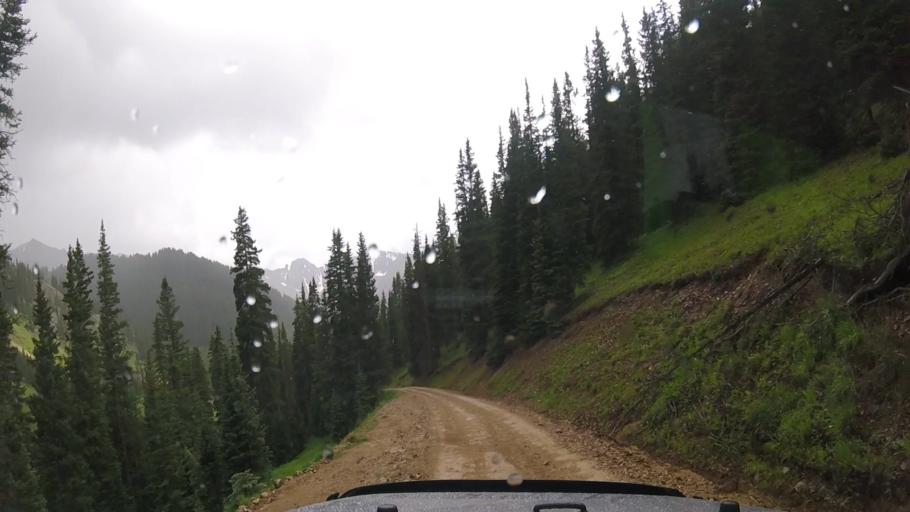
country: US
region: Colorado
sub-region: San Juan County
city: Silverton
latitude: 37.9013
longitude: -107.6471
